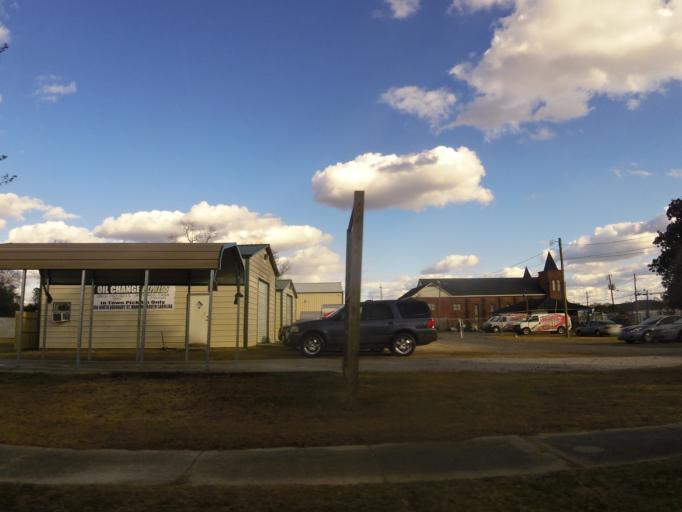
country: US
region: South Carolina
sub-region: Clarendon County
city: Manning
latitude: 33.6972
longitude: -80.2135
